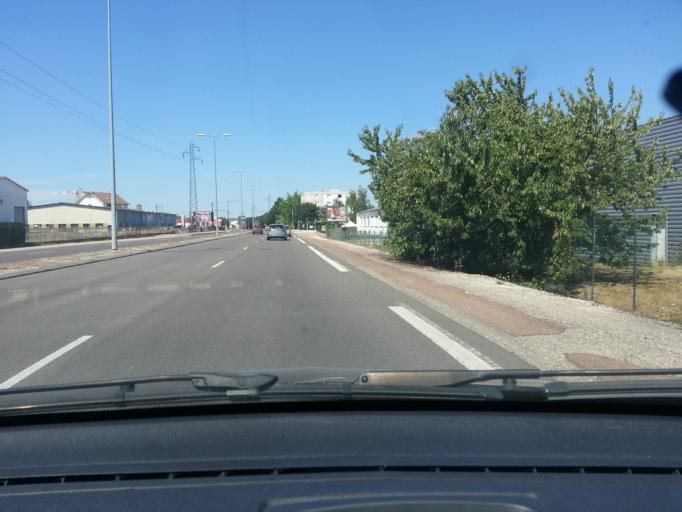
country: FR
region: Bourgogne
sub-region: Departement de la Cote-d'Or
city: Dijon
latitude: 47.2988
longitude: 5.0239
